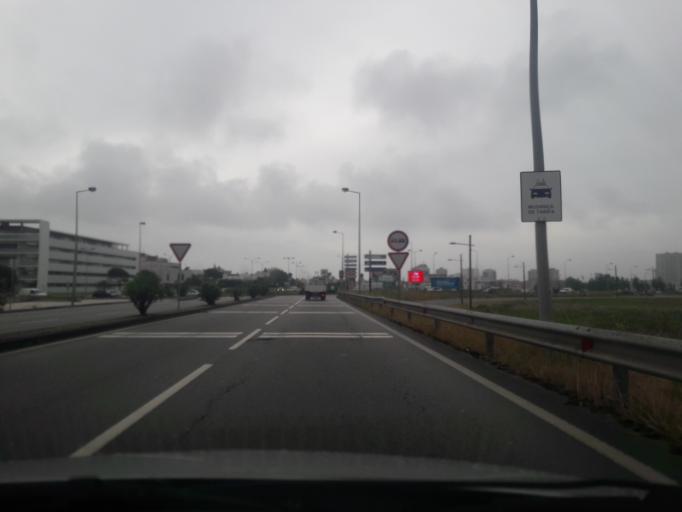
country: PT
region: Porto
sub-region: Povoa de Varzim
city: Povoa de Varzim
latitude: 41.3948
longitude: -8.7567
